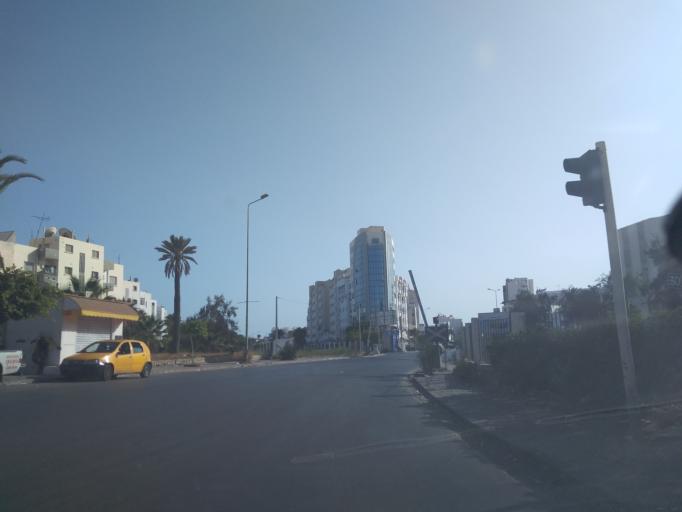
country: TN
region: Safaqis
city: Sfax
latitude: 34.7449
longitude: 10.7653
